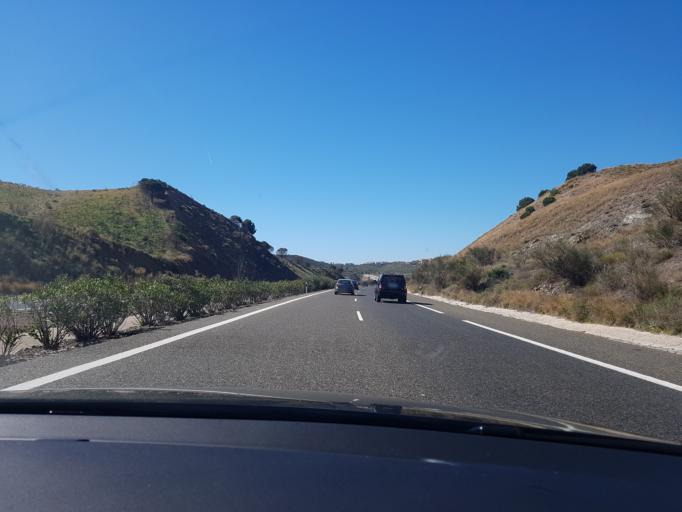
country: ES
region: Andalusia
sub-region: Provincia de Malaga
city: Fuengirola
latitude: 36.5201
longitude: -4.6878
